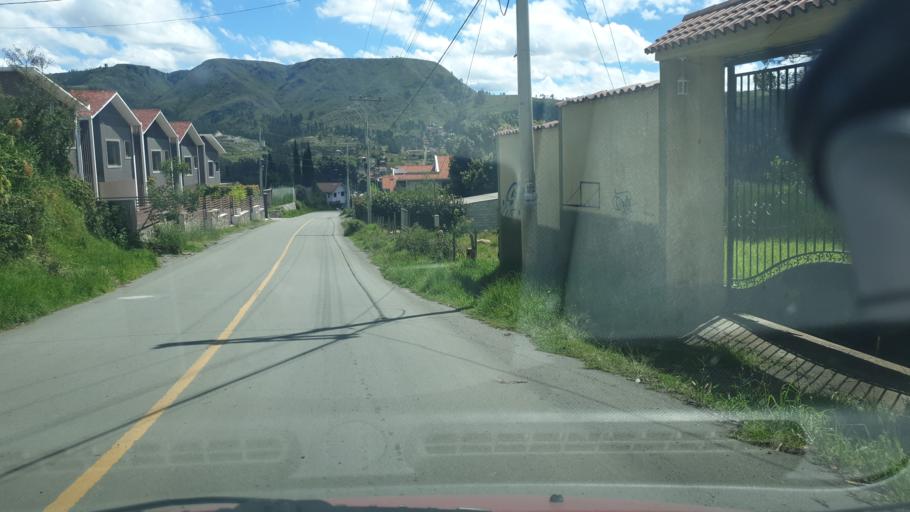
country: EC
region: Azuay
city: Llacao
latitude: -2.8574
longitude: -78.9085
